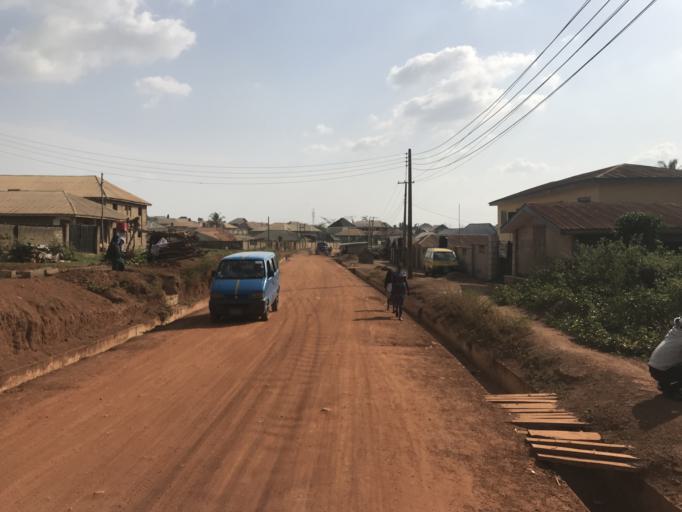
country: NG
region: Osun
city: Osogbo
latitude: 7.8135
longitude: 4.5601
